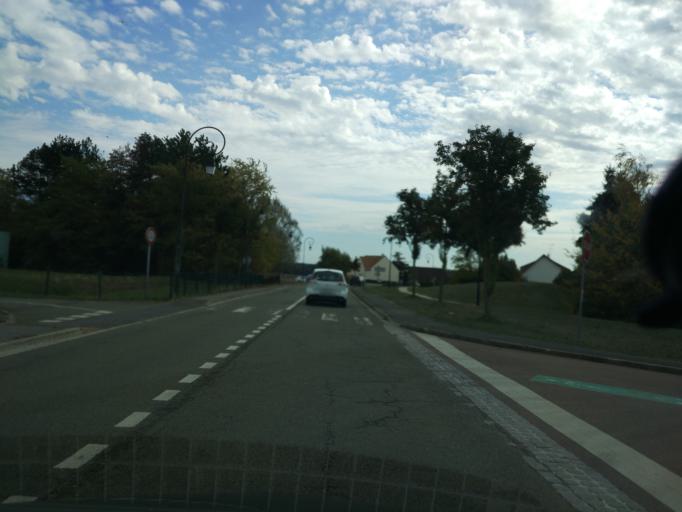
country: FR
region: Ile-de-France
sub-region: Departement de l'Essonne
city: Gometz-la-Ville
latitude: 48.6702
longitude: 2.1280
